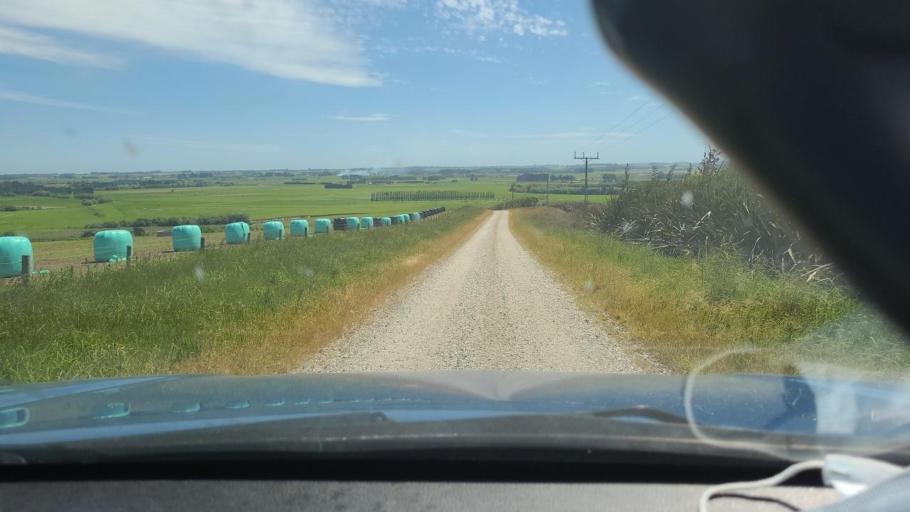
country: NZ
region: Southland
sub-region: Gore District
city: Gore
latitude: -46.3832
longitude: 168.8265
